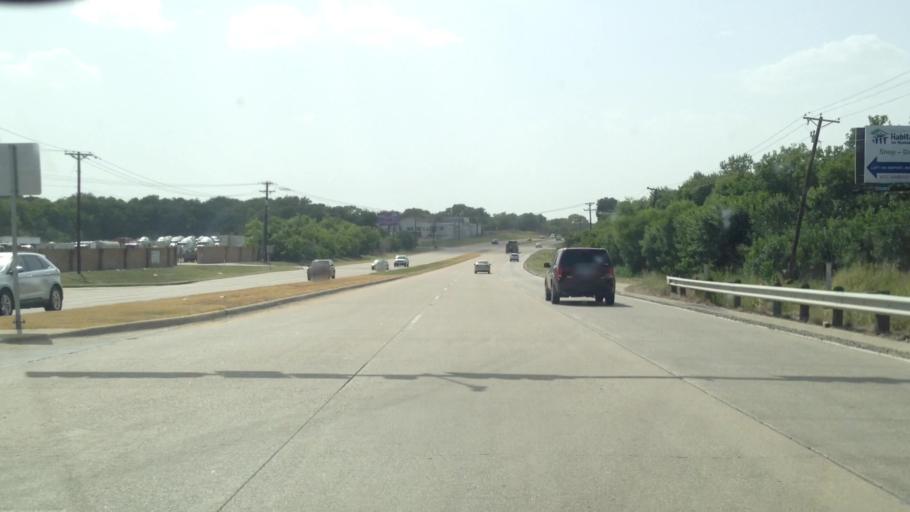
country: US
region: Texas
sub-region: Collin County
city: McKinney
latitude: 33.2045
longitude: -96.5988
